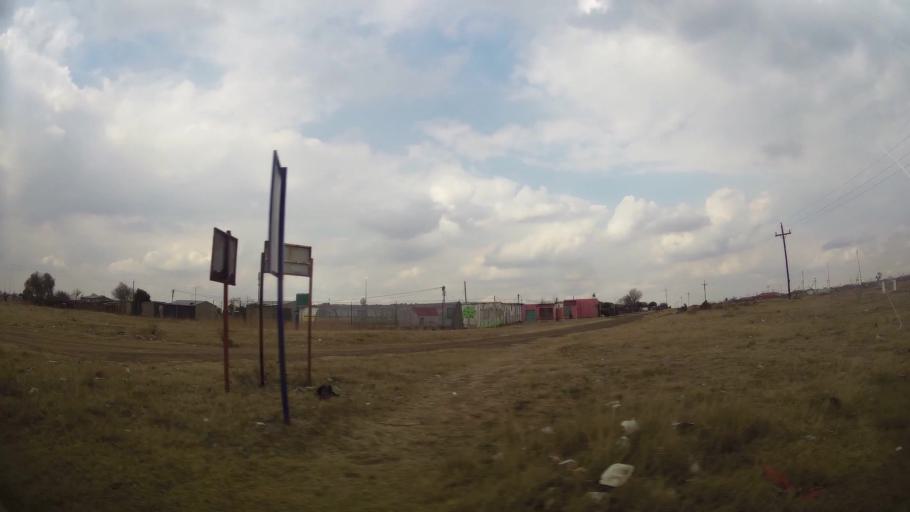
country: ZA
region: Orange Free State
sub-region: Fezile Dabi District Municipality
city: Sasolburg
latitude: -26.8567
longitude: 27.8722
